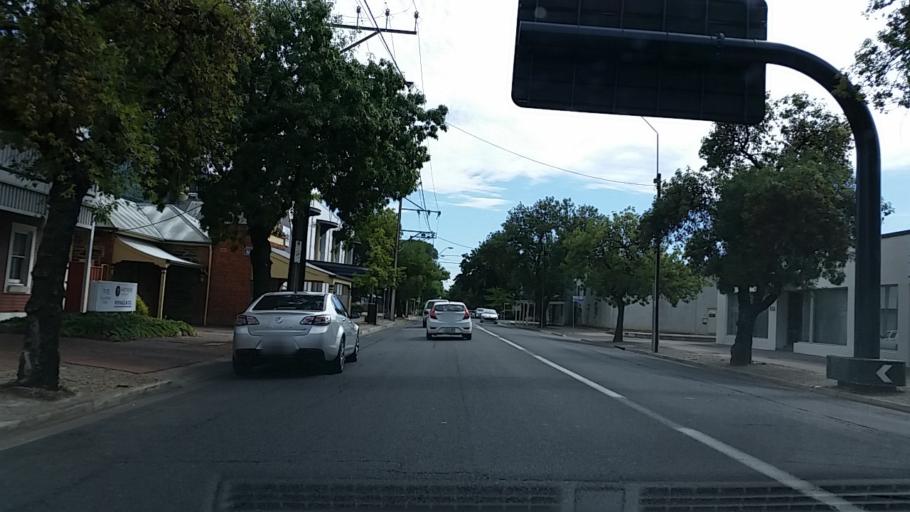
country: AU
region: South Australia
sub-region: Norwood Payneham St Peters
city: Trinity Gardens
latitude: -34.9258
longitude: 138.6235
